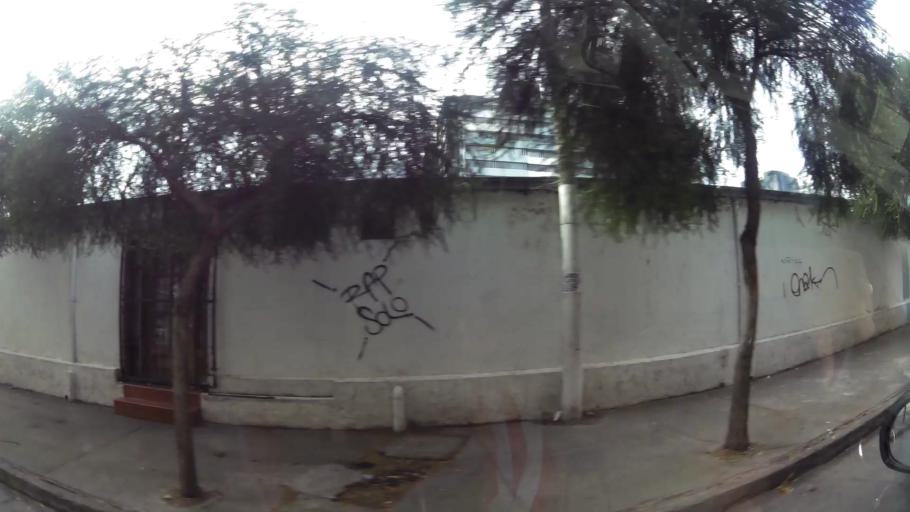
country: EC
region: Pichincha
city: Quito
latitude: -0.1765
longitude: -78.4870
